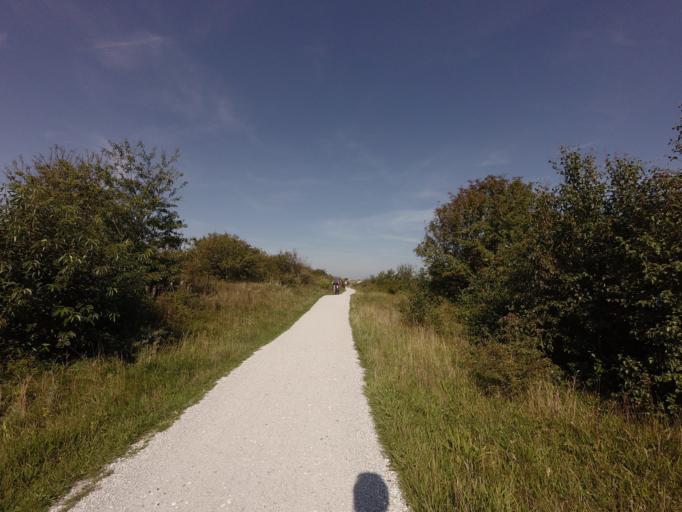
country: NL
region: Friesland
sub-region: Gemeente Schiermonnikoog
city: Schiermonnikoog
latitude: 53.4728
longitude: 6.1433
